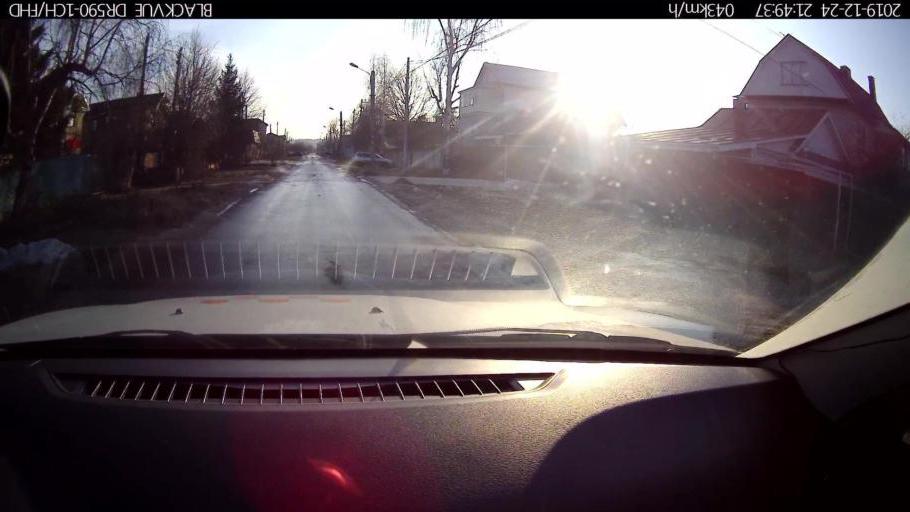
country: RU
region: Nizjnij Novgorod
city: Burevestnik
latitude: 56.2247
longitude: 43.8414
